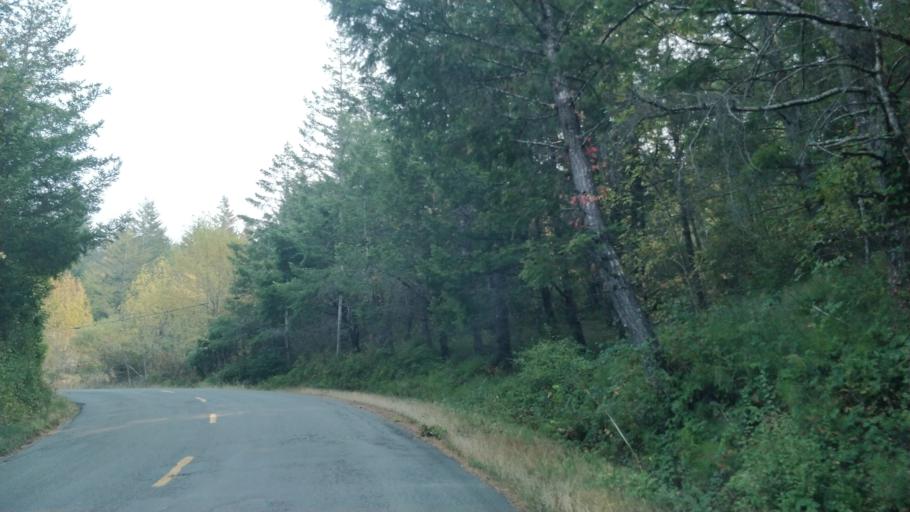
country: US
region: California
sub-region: Humboldt County
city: Rio Dell
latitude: 40.3031
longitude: -124.2546
